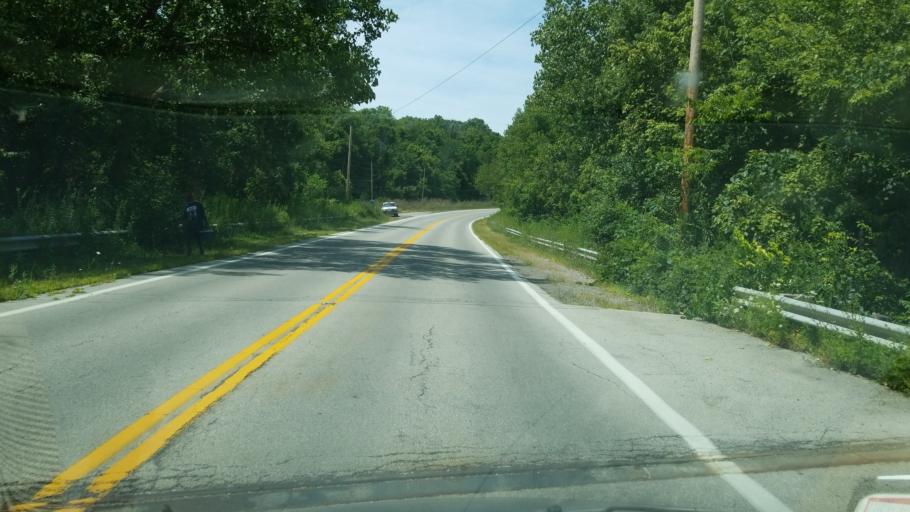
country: US
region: Ohio
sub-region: Franklin County
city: Lake Darby
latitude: 39.8483
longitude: -83.2033
